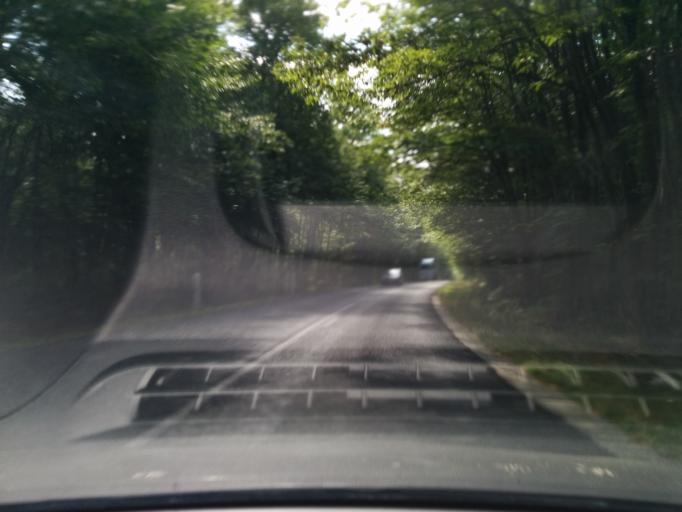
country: FR
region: Centre
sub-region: Departement du Cher
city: Neuvy-sur-Barangeon
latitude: 47.3267
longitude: 2.3419
